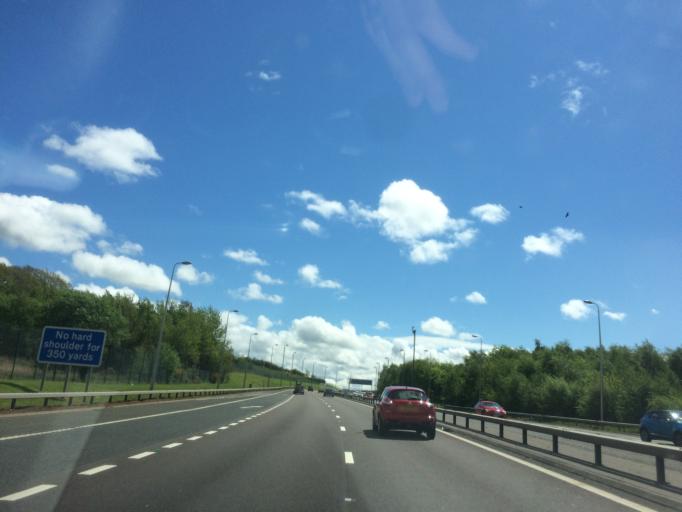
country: GB
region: Scotland
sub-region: East Renfrewshire
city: Giffnock
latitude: 55.8173
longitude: -4.3368
